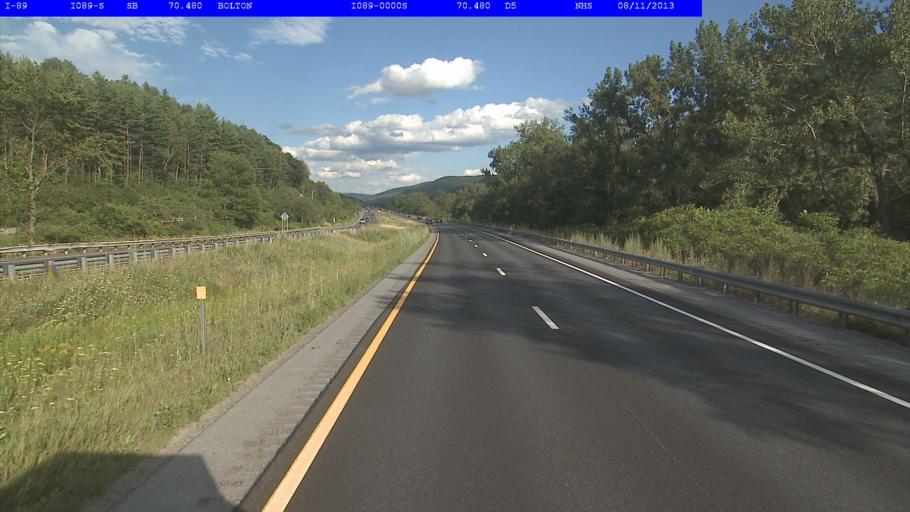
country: US
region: Vermont
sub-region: Washington County
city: Waterbury
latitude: 44.3724
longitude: -72.8774
